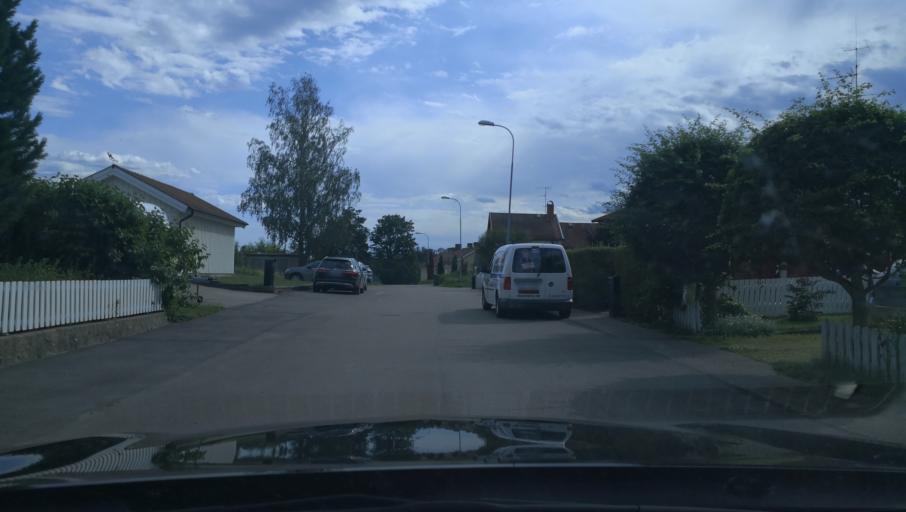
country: SE
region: Vaestmanland
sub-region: Fagersta Kommun
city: Fagersta
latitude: 59.9869
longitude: 15.8277
